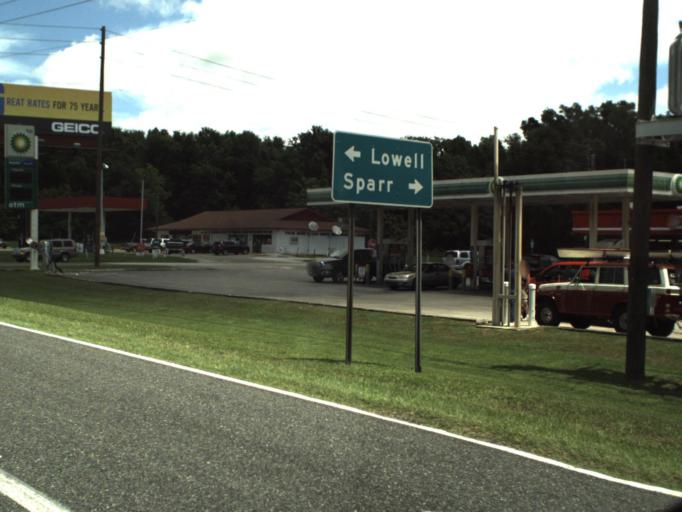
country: US
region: Florida
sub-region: Marion County
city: Citra
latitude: 29.3374
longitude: -82.1515
